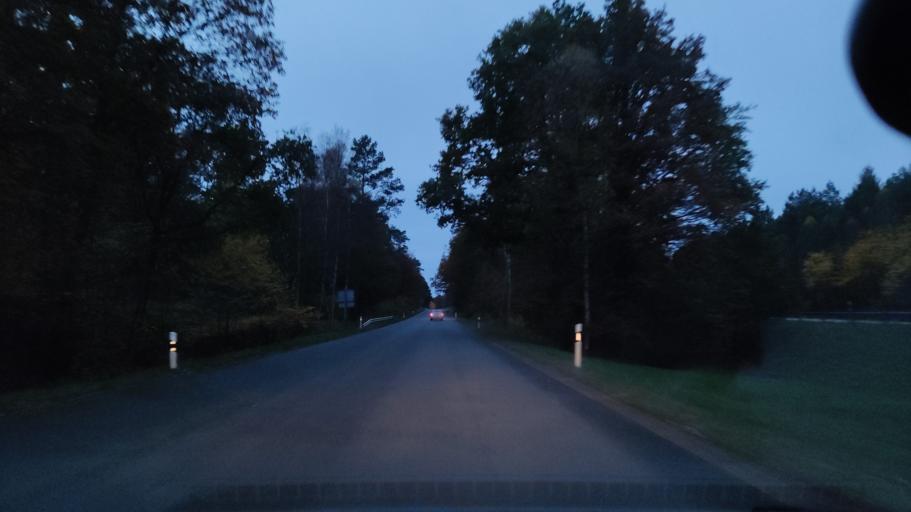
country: DE
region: Lower Saxony
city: Munster
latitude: 53.0128
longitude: 10.0980
